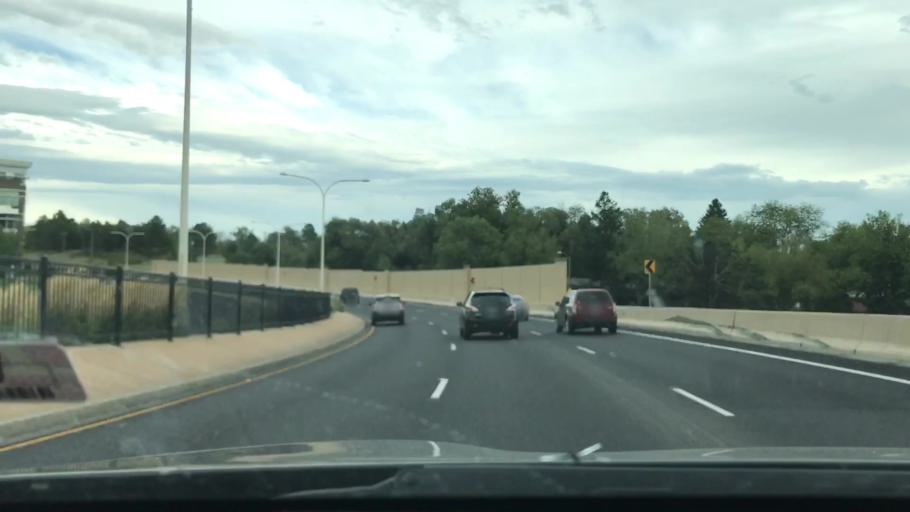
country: US
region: Colorado
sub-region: El Paso County
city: Colorado Springs
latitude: 38.8920
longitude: -104.8056
